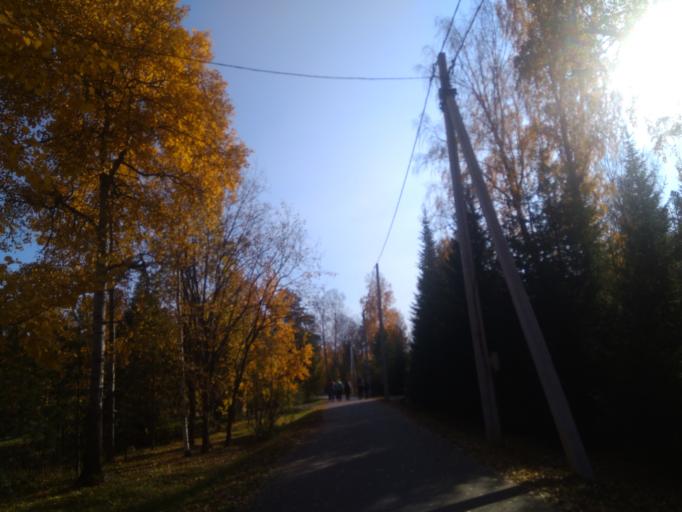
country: RU
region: Sverdlovsk
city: Mikhaylovsk
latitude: 56.5238
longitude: 59.2312
